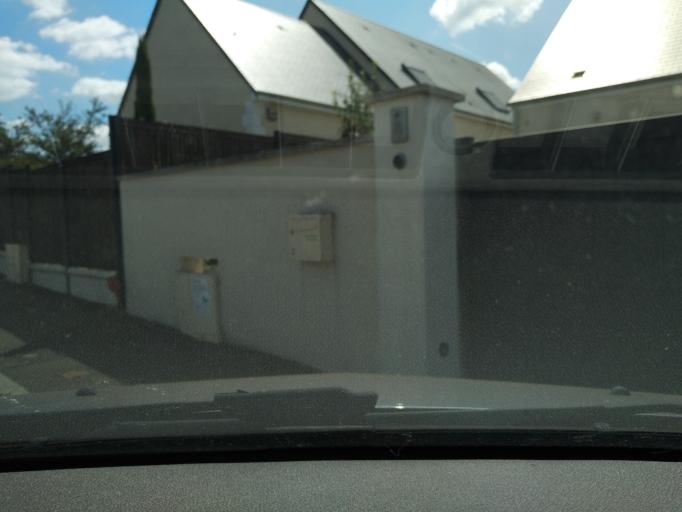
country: FR
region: Centre
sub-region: Departement d'Indre-et-Loire
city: Chanceaux-sur-Choisille
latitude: 47.4556
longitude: 0.7042
